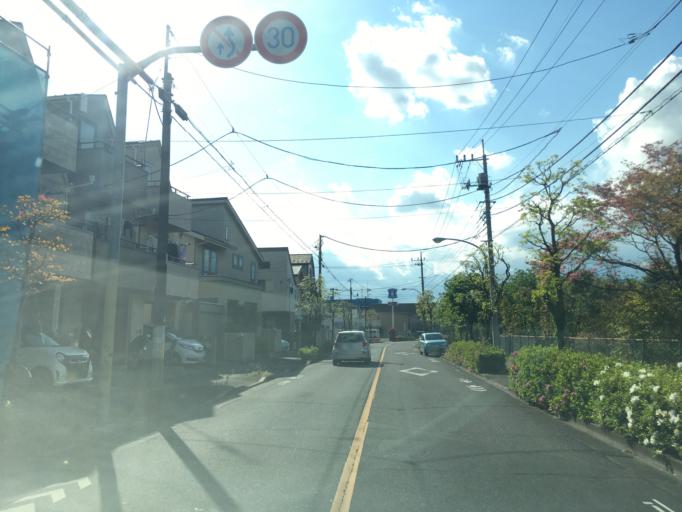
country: JP
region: Tokyo
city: Kokubunji
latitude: 35.7013
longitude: 139.4921
